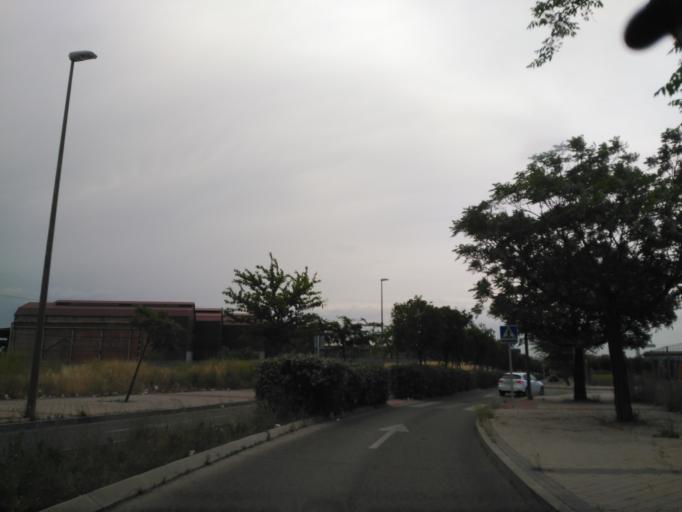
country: ES
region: Madrid
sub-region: Provincia de Madrid
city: Villaverde
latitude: 40.3373
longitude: -3.7199
